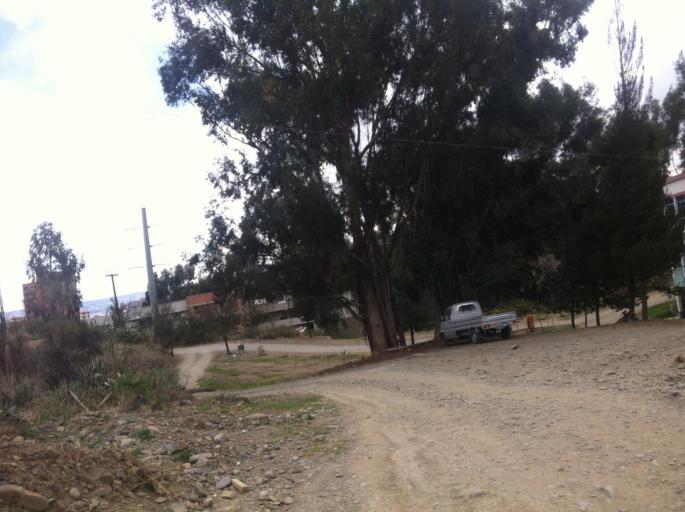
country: BO
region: La Paz
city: La Paz
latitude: -16.5387
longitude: -68.0635
